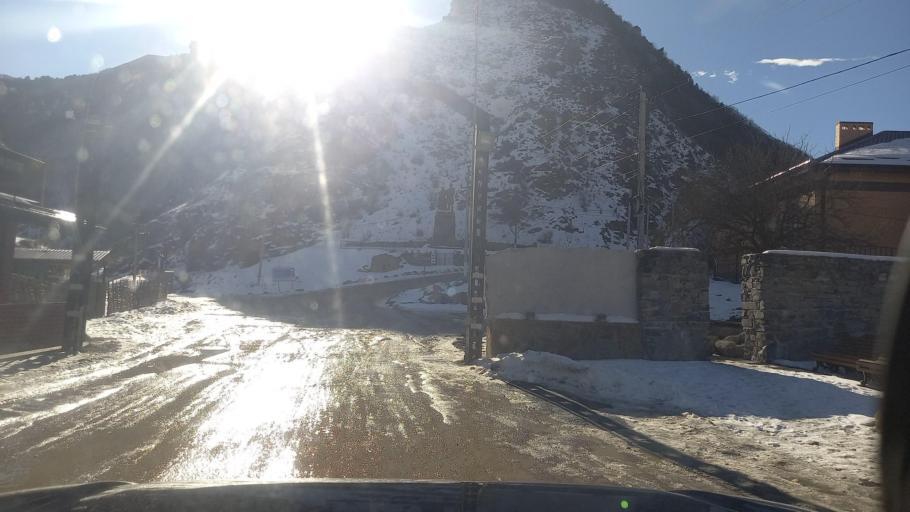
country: RU
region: North Ossetia
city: Chikola
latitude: 42.9815
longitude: 43.7762
